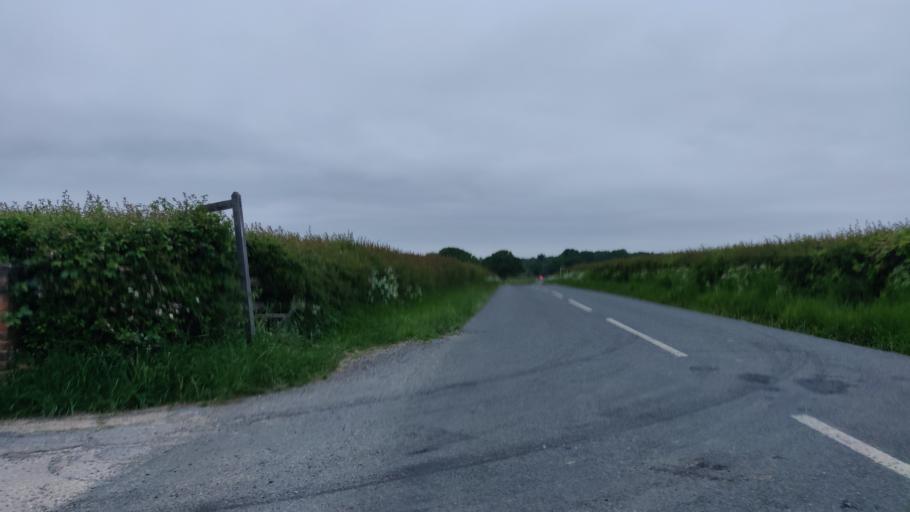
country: GB
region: England
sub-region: West Sussex
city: Partridge Green
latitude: 50.9741
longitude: -0.3020
